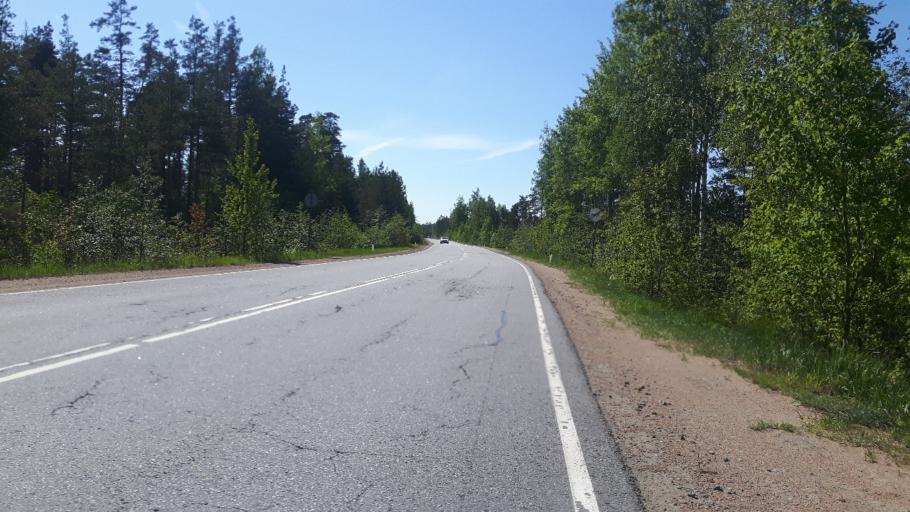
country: RU
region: Leningrad
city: Sista-Palkino
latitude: 59.7698
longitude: 28.7800
